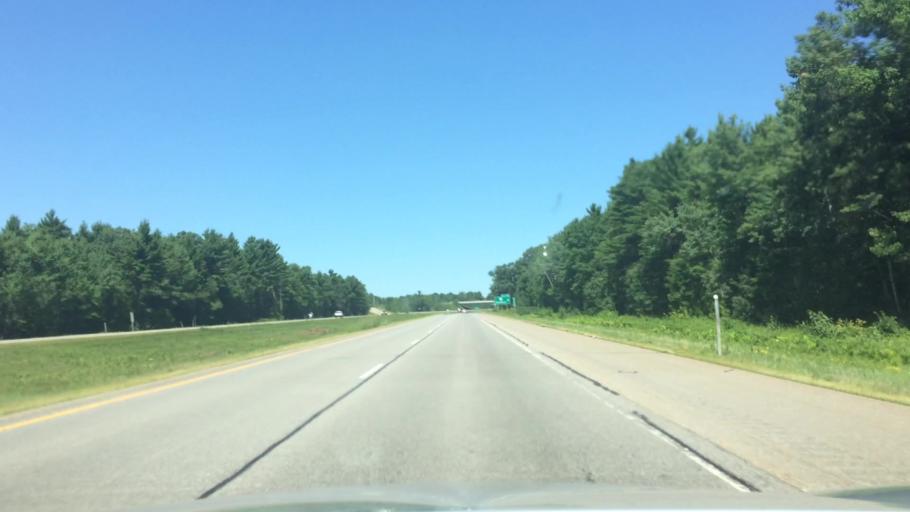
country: US
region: Wisconsin
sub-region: Marathon County
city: Mosinee
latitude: 44.7232
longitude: -89.6711
